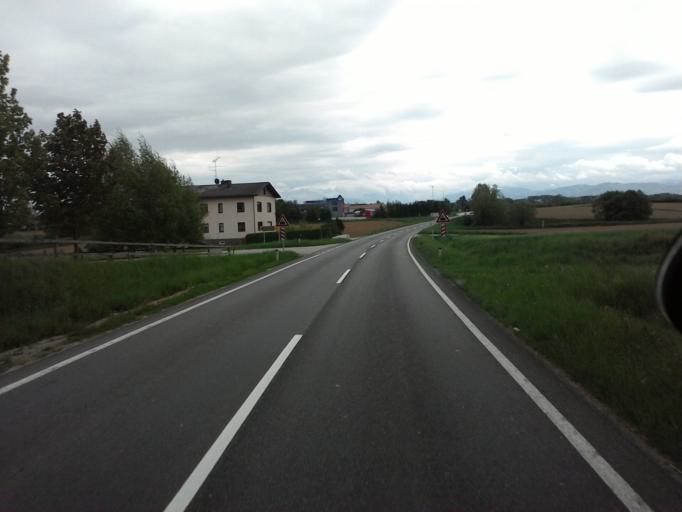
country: AT
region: Upper Austria
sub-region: Wels-Land
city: Sattledt
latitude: 48.0505
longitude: 14.0578
